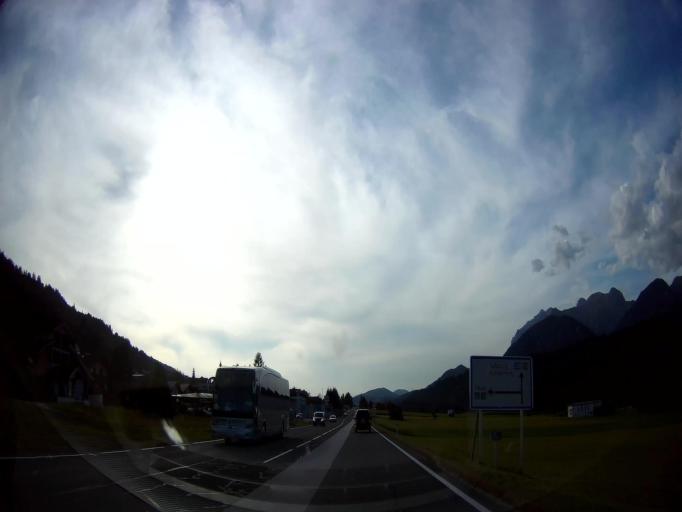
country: AT
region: Styria
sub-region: Politischer Bezirk Liezen
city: Haus im Ennstal
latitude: 47.4122
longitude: 13.7755
